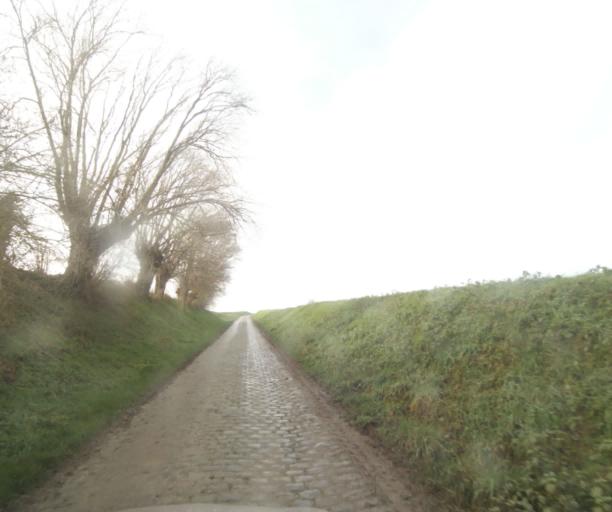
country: FR
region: Nord-Pas-de-Calais
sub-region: Departement du Nord
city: Maing
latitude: 50.2986
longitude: 3.4687
